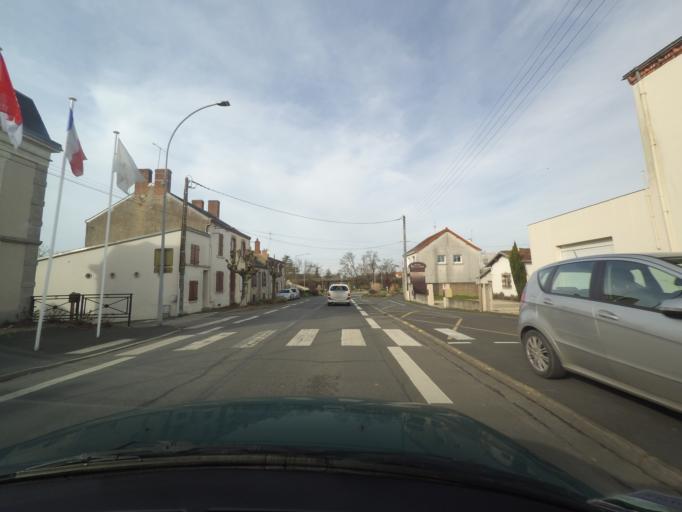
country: FR
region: Pays de la Loire
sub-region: Departement de la Vendee
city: Montaigu
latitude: 46.9817
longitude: -1.3173
